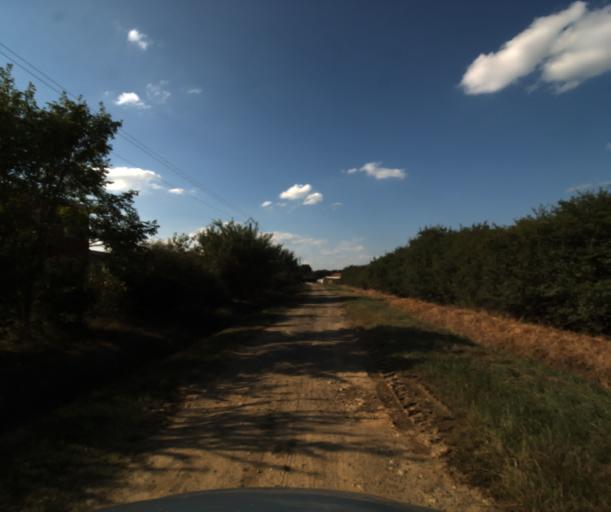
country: FR
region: Midi-Pyrenees
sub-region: Departement de la Haute-Garonne
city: Saint-Lys
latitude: 43.5119
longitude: 1.2007
